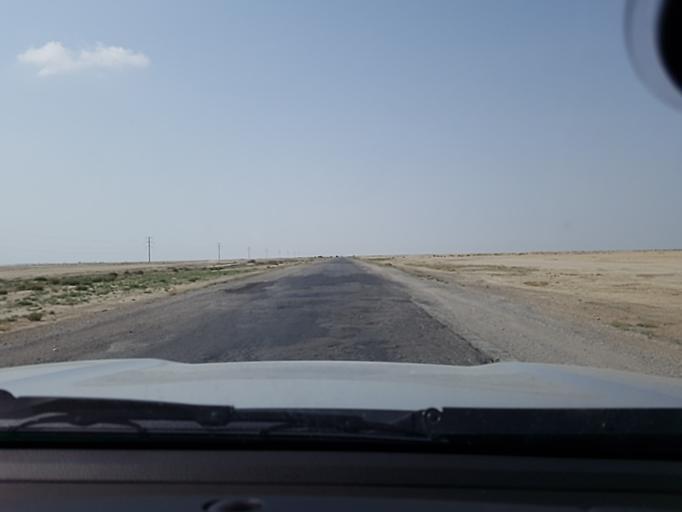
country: TM
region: Balkan
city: Gumdag
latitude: 38.8936
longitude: 54.5928
